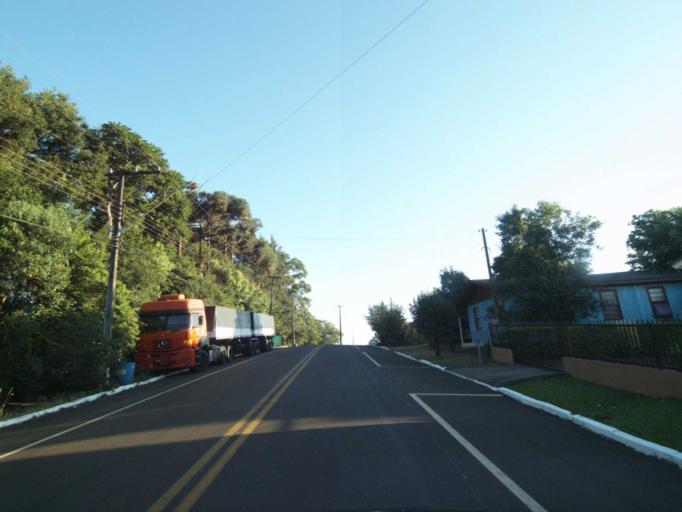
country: BR
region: Parana
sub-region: Coronel Vivida
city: Coronel Vivida
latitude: -25.9743
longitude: -52.8151
